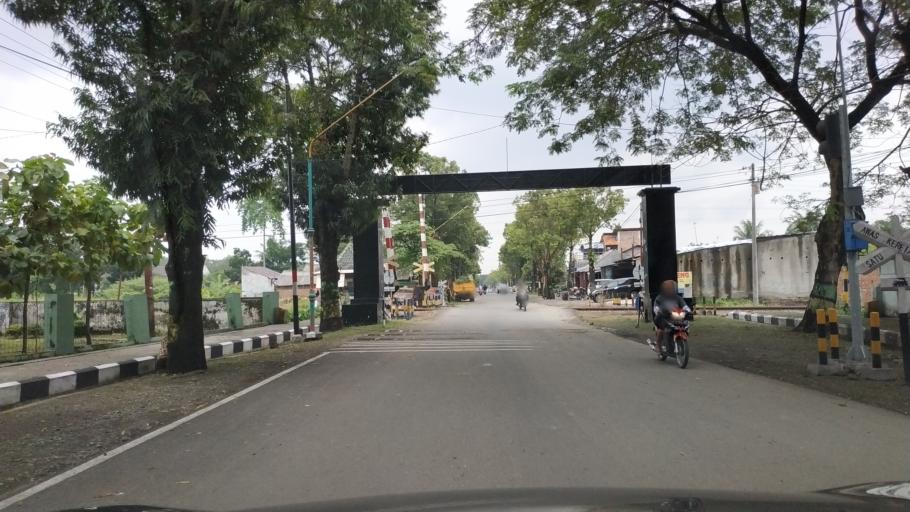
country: ID
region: Central Java
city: Slawi
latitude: -6.9939
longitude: 109.1318
